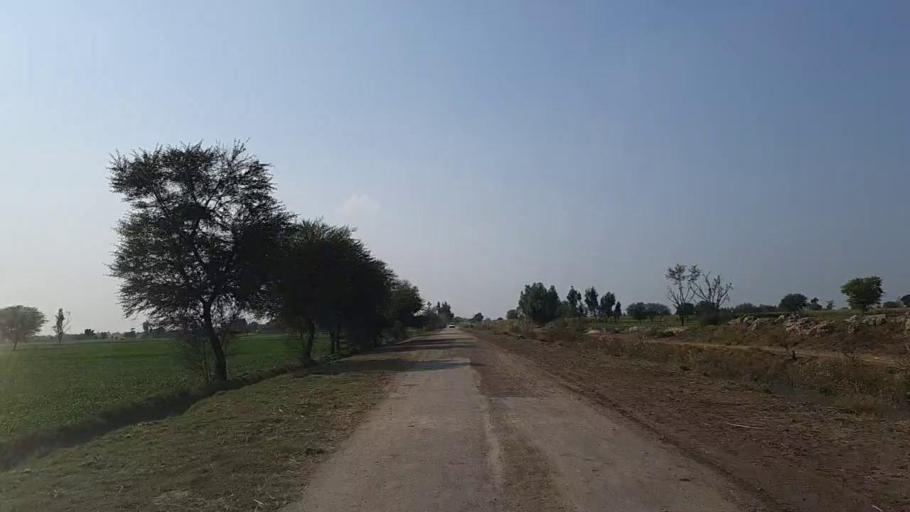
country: PK
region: Sindh
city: Jam Sahib
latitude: 26.2883
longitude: 68.5734
